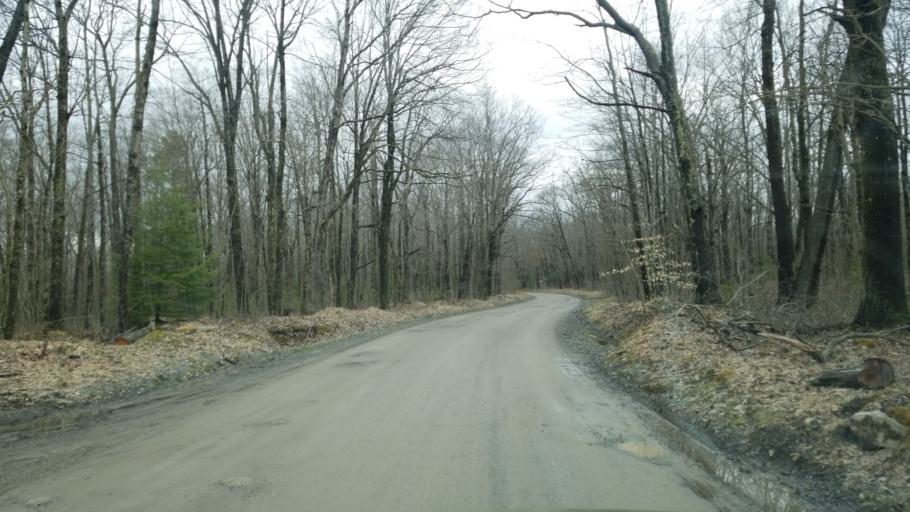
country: US
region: Pennsylvania
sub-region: Clearfield County
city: Shiloh
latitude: 41.1700
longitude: -78.3417
